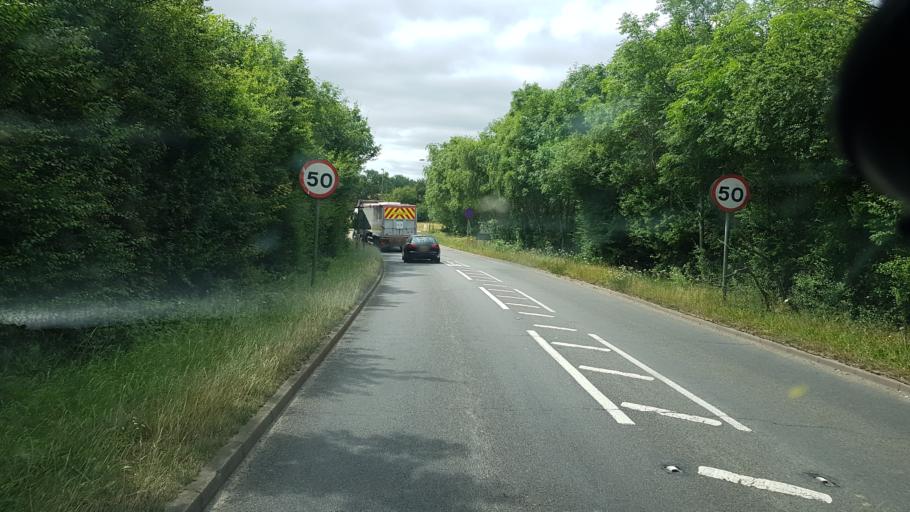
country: GB
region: England
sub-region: Surrey
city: Godstone
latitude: 51.2366
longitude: -0.0485
